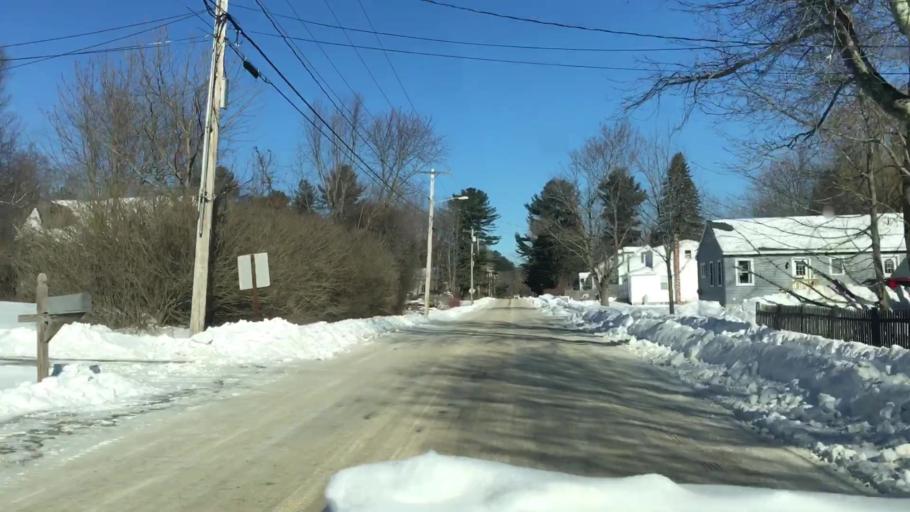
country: US
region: Maine
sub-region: Sagadahoc County
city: Topsham
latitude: 43.9222
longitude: -69.9727
